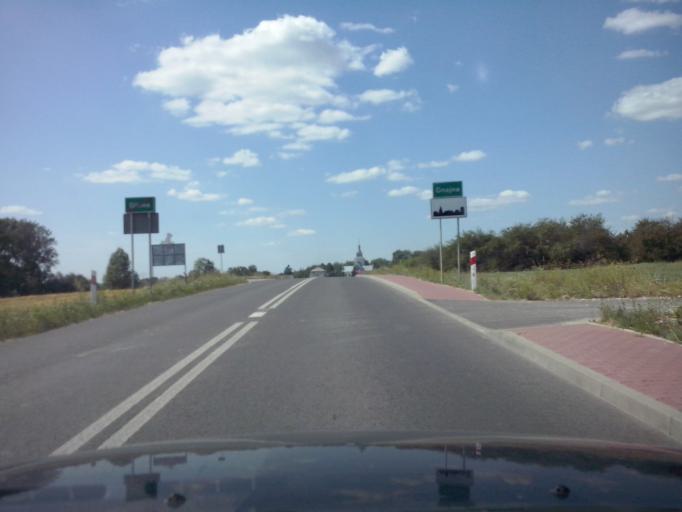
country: PL
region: Swietokrzyskie
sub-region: Powiat buski
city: Gnojno
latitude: 50.6000
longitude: 20.8574
